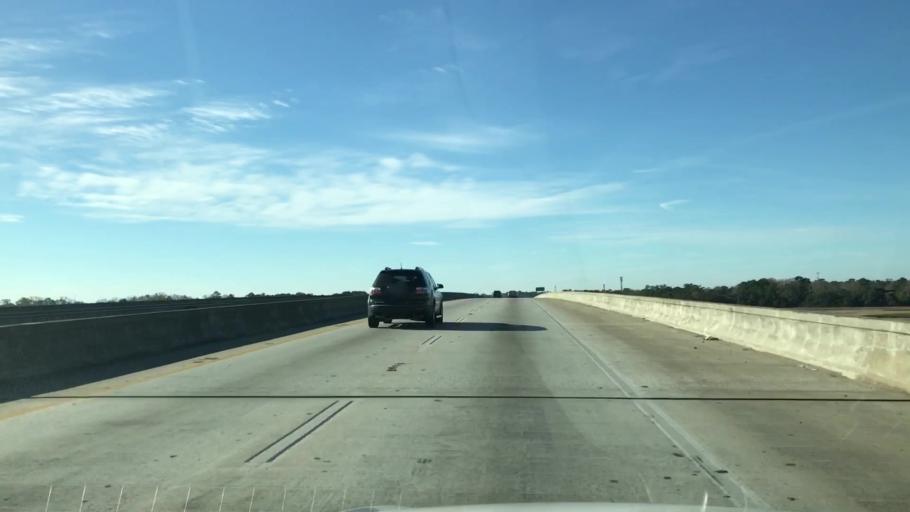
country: US
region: South Carolina
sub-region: Charleston County
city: North Charleston
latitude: 32.8356
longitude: -80.0245
